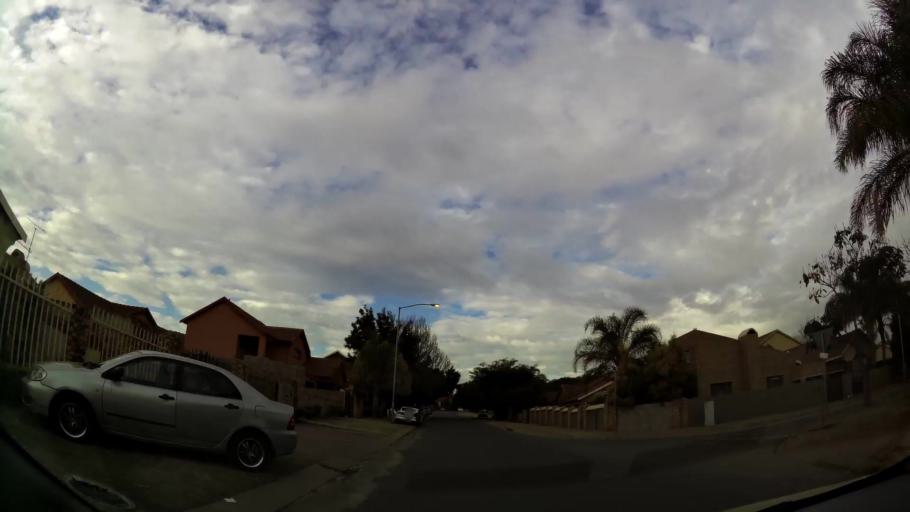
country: ZA
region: Gauteng
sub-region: City of Tshwane Metropolitan Municipality
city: Pretoria
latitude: -25.7024
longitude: 28.3061
